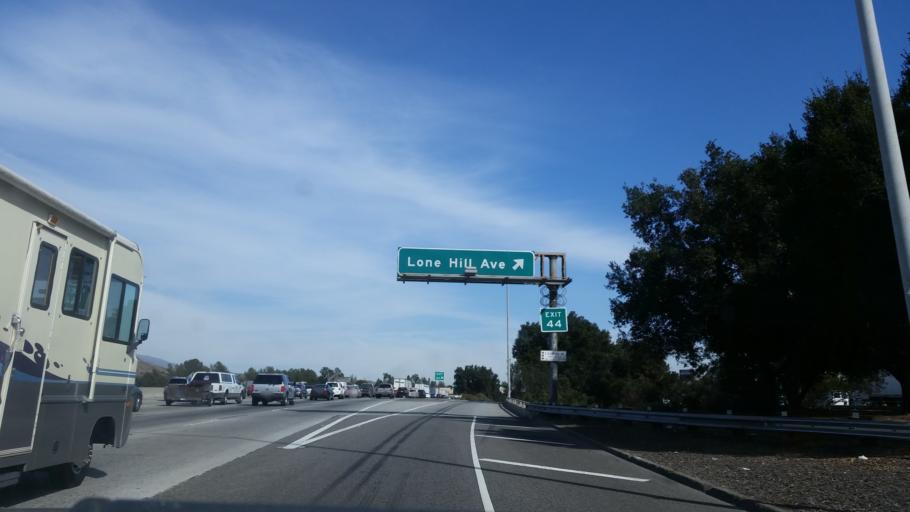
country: US
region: California
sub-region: Los Angeles County
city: Charter Oak
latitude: 34.1209
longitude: -117.8323
